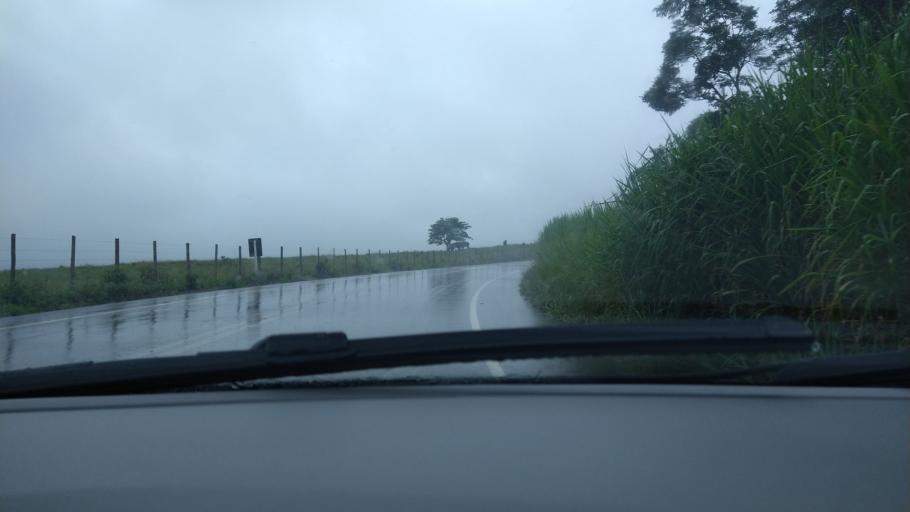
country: BR
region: Minas Gerais
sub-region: Ponte Nova
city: Ponte Nova
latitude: -20.5488
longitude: -42.8848
